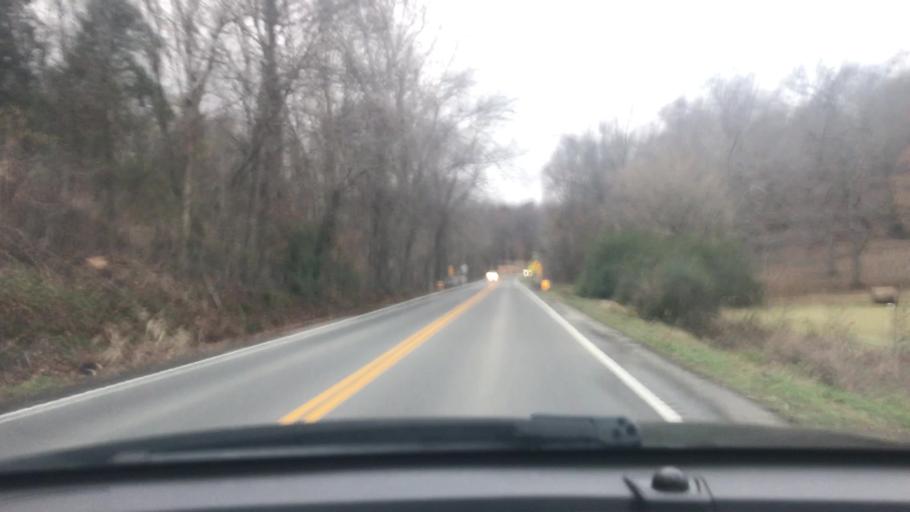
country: US
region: Tennessee
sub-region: Dickson County
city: Charlotte
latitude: 36.2414
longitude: -87.3460
